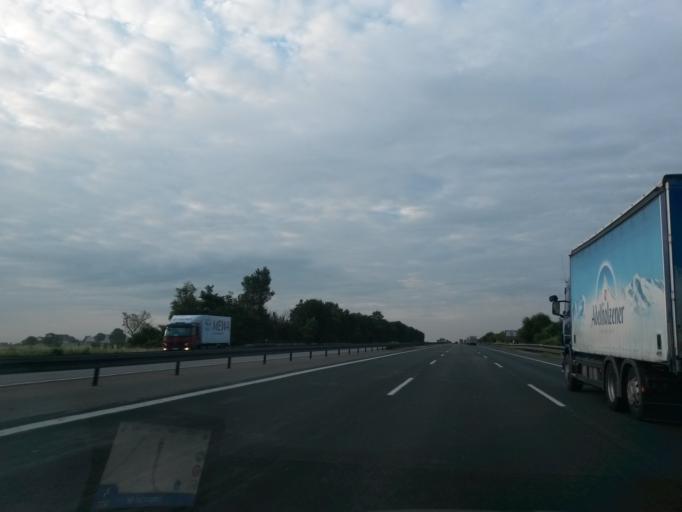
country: DE
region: Bavaria
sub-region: Regierungsbezirk Mittelfranken
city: Hilpoltstein
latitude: 49.1873
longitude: 11.2514
